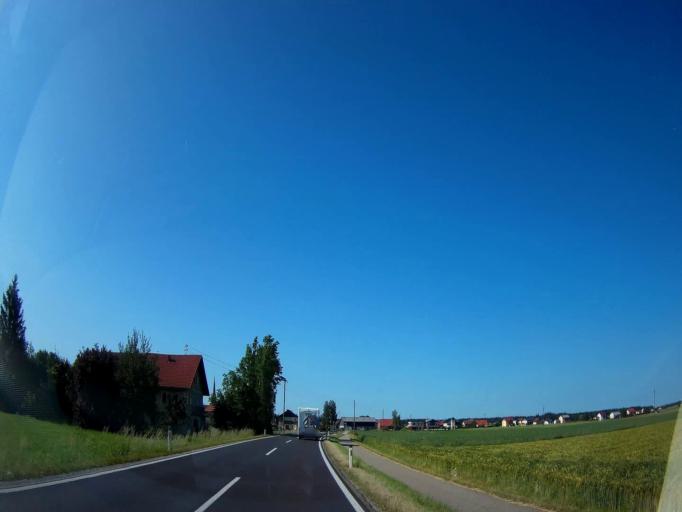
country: AT
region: Upper Austria
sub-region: Politischer Bezirk Braunau am Inn
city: Braunau am Inn
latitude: 48.1725
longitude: 13.0495
